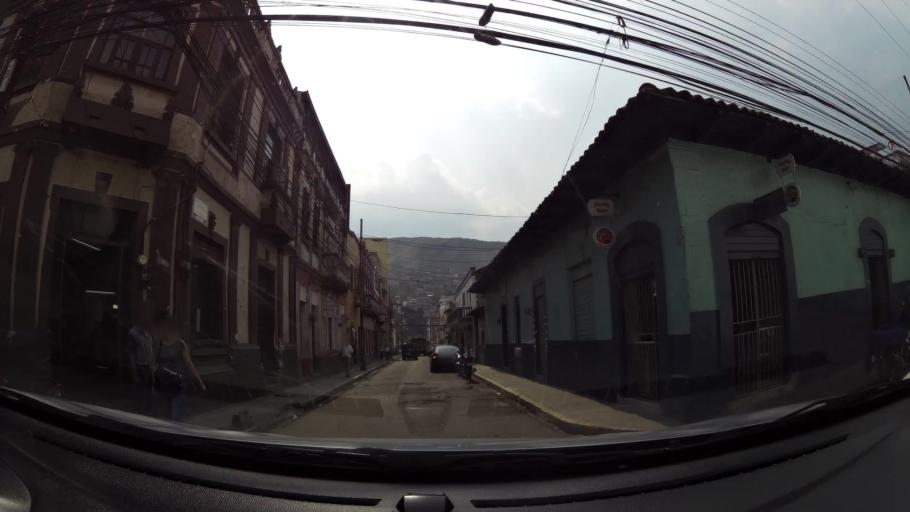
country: HN
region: Francisco Morazan
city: Tegucigalpa
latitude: 14.1079
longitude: -87.2075
